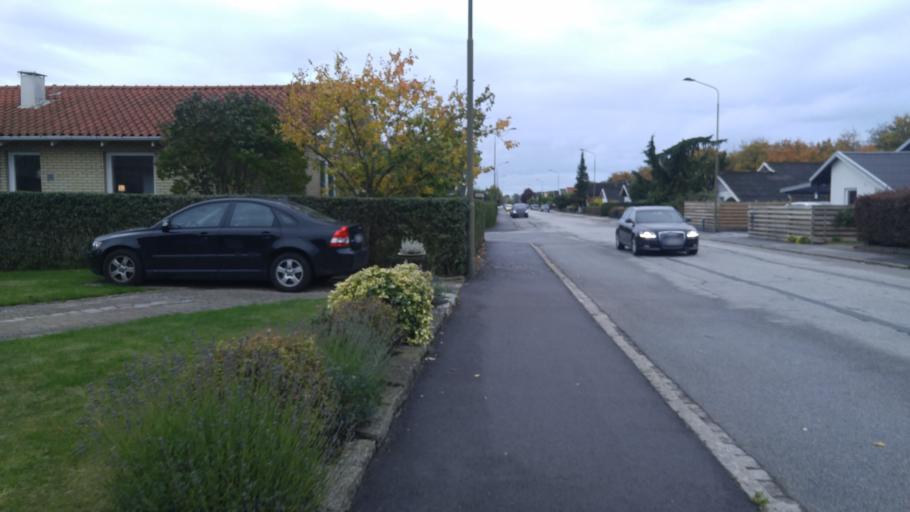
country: SE
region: Skane
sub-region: Malmo
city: Bunkeflostrand
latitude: 55.5741
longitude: 12.9503
